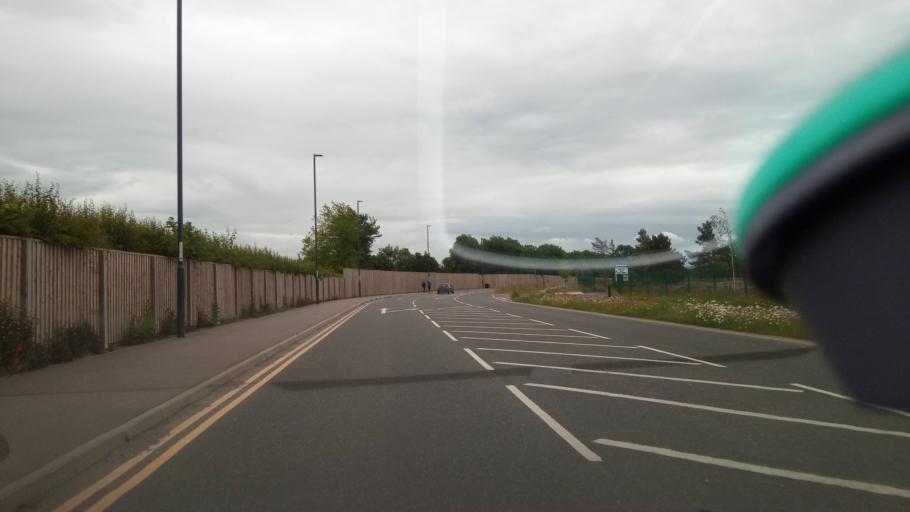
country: GB
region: England
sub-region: Derby
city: Derby
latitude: 52.8887
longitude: -1.4588
